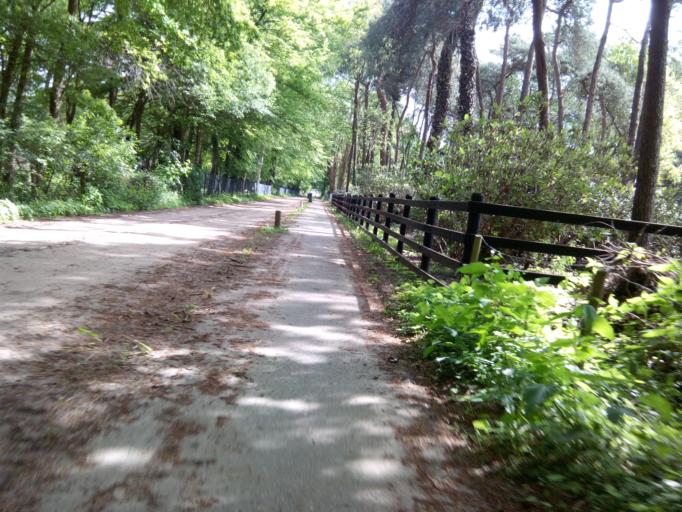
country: NL
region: Gelderland
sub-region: Gemeente Ede
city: Ede
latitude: 52.0661
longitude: 5.6550
